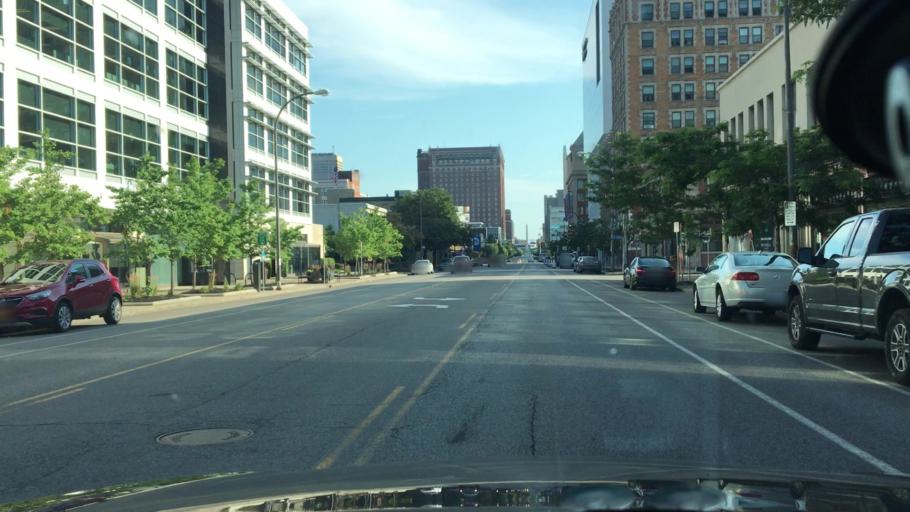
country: US
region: New York
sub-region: Erie County
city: Buffalo
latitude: 42.8928
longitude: -78.8761
